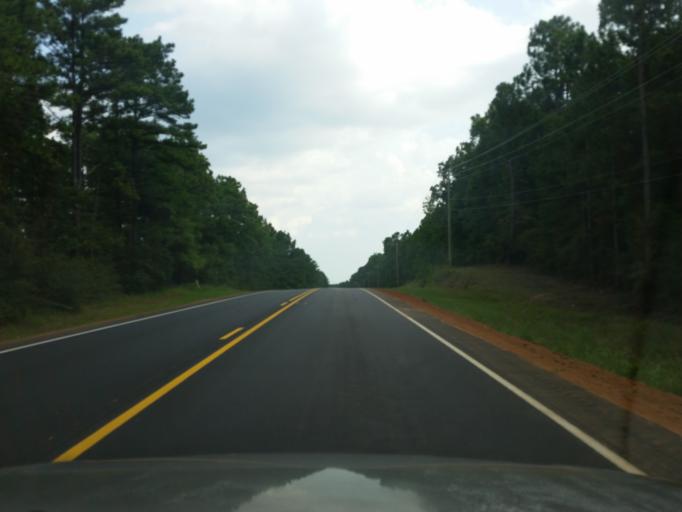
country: US
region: Alabama
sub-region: Baldwin County
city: Spanish Fort
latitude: 30.7227
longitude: -87.9009
